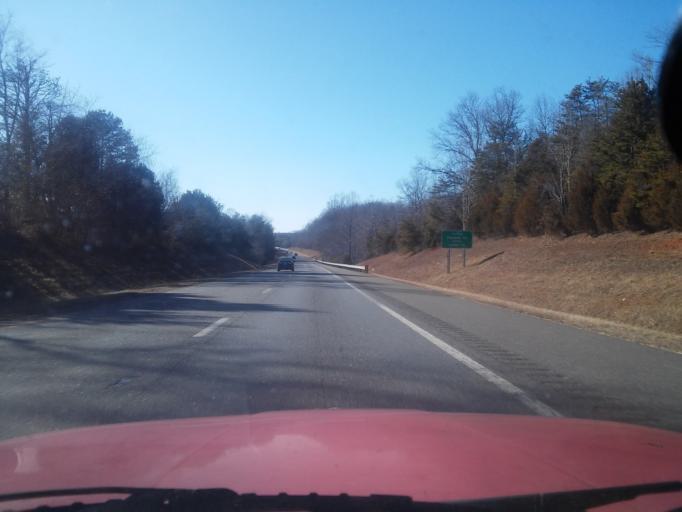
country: US
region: Virginia
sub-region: Fluvanna County
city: Lake Monticello
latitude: 37.9973
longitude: -78.2879
